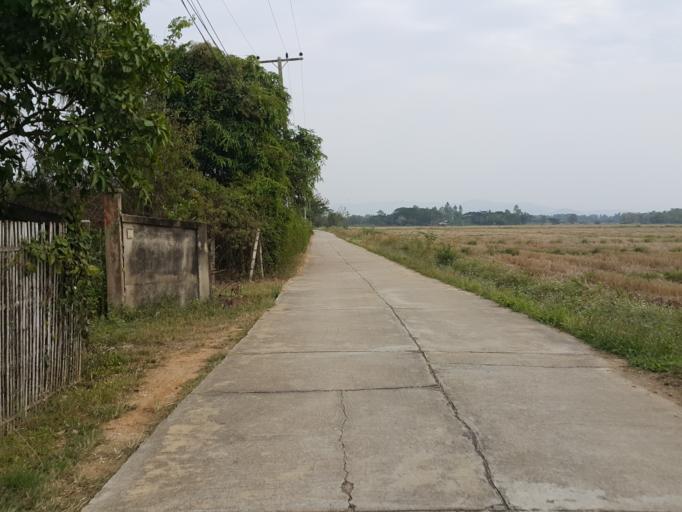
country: TH
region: Chiang Mai
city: San Kamphaeng
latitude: 18.8265
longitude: 99.1286
